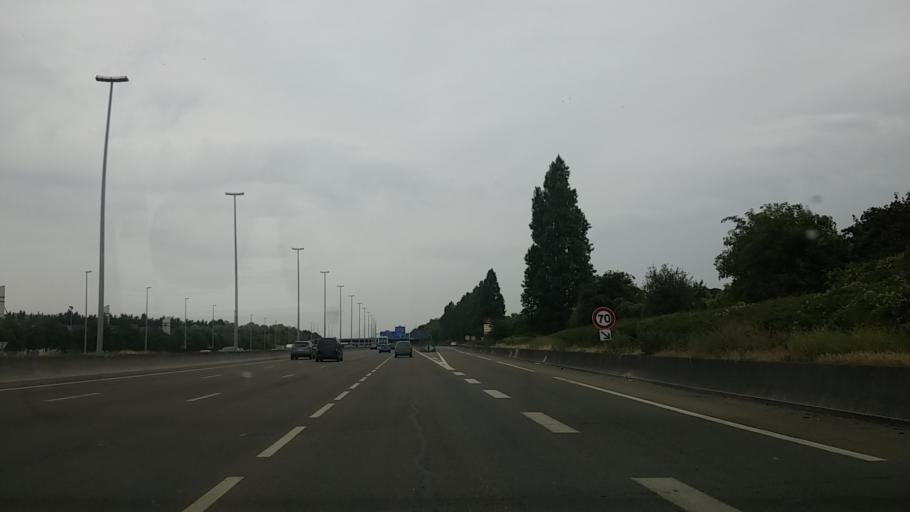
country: FR
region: Ile-de-France
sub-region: Departement de Seine-Saint-Denis
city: Le Blanc-Mesnil
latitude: 48.9576
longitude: 2.4630
